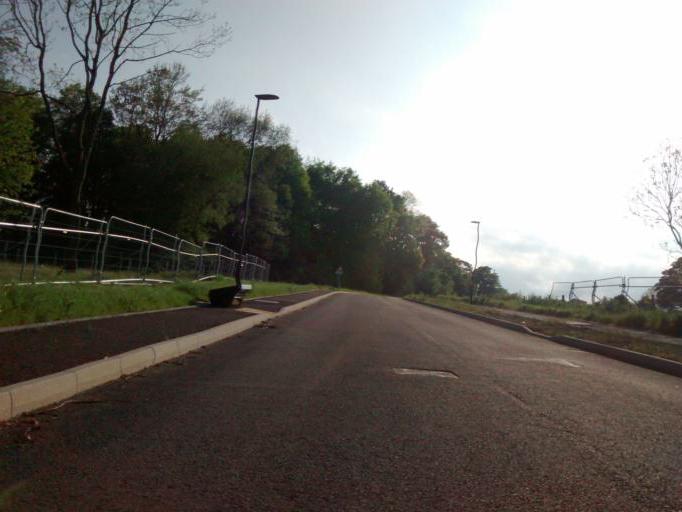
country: GB
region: England
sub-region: County Durham
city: Durham
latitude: 54.7615
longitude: -1.5838
